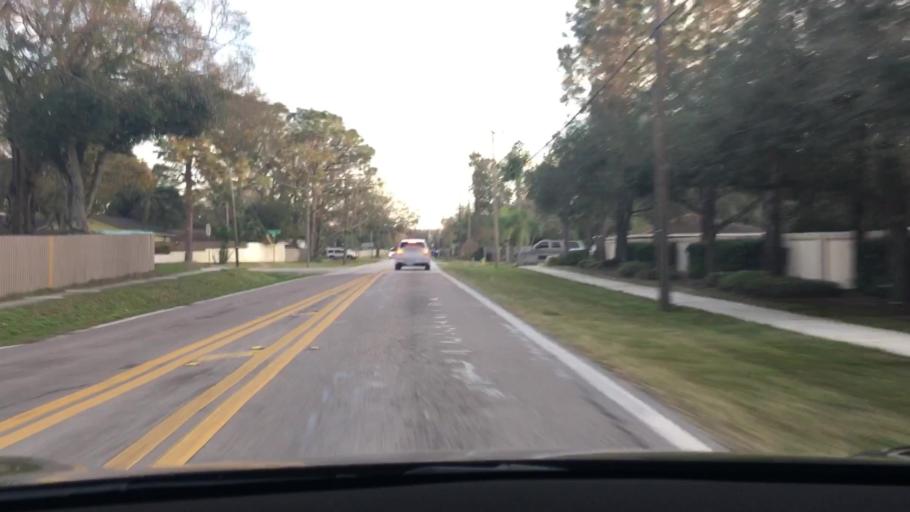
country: US
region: Florida
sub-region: Hillsborough County
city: Greater Northdale
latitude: 28.0907
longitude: -82.5399
